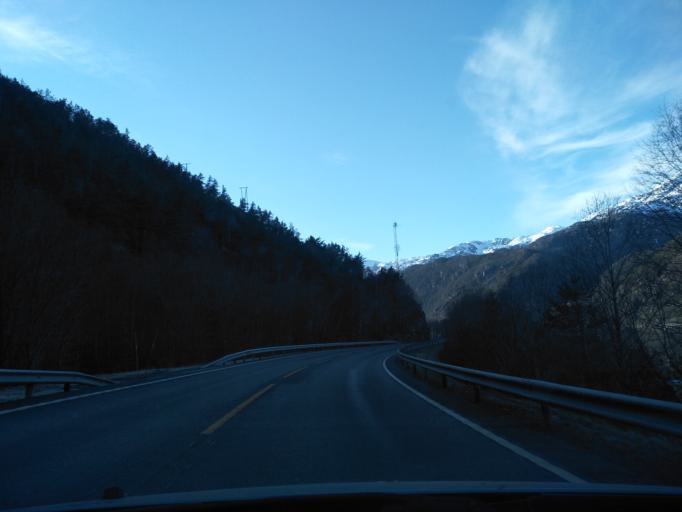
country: NO
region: Rogaland
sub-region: Sauda
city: Sauda
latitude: 59.8365
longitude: 6.3043
